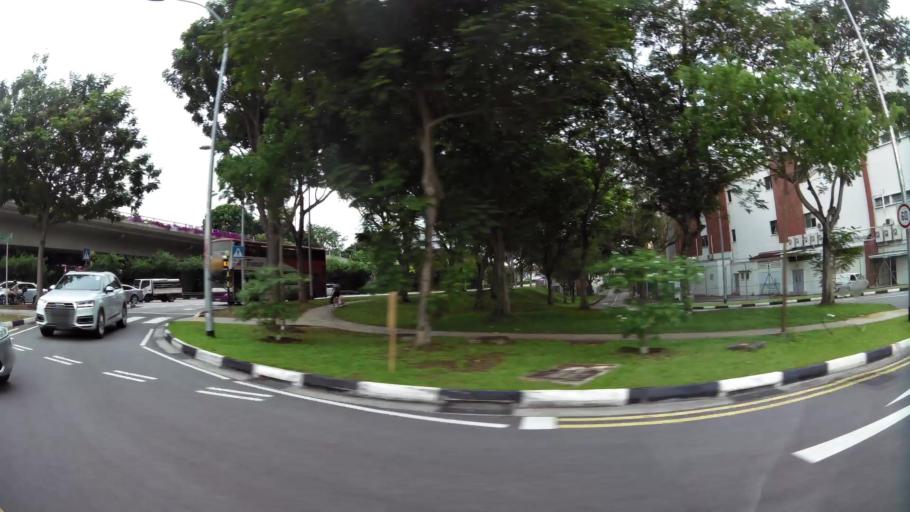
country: SG
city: Singapore
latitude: 1.3522
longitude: 103.8771
